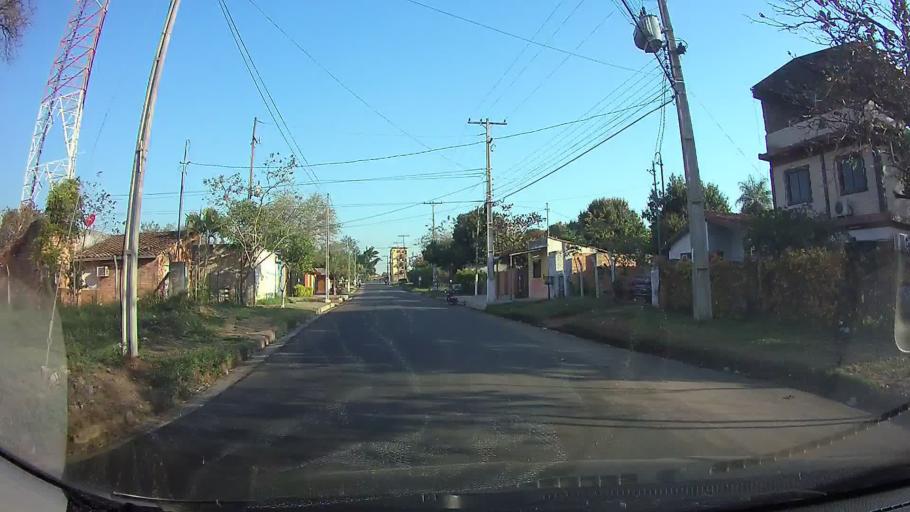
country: PY
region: Central
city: San Lorenzo
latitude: -25.2589
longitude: -57.4805
